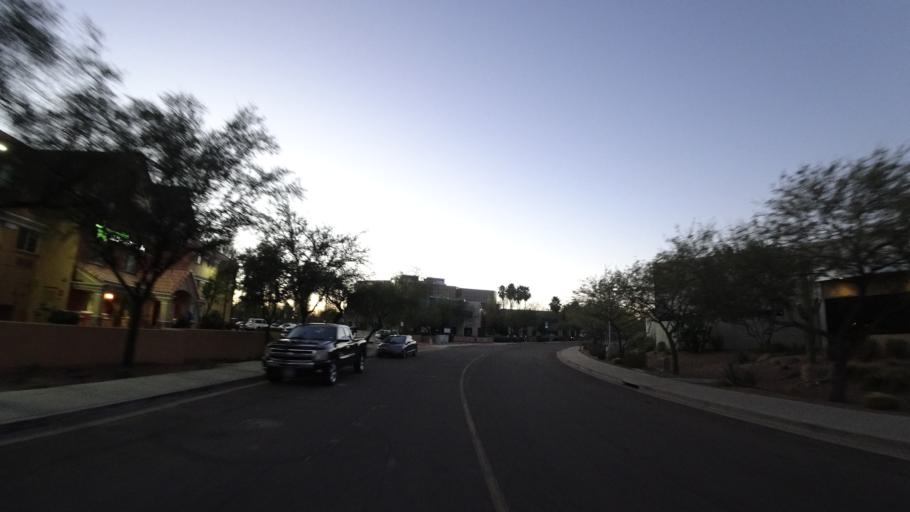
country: US
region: Arizona
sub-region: Maricopa County
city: Tempe Junction
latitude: 33.4122
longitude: -111.9722
